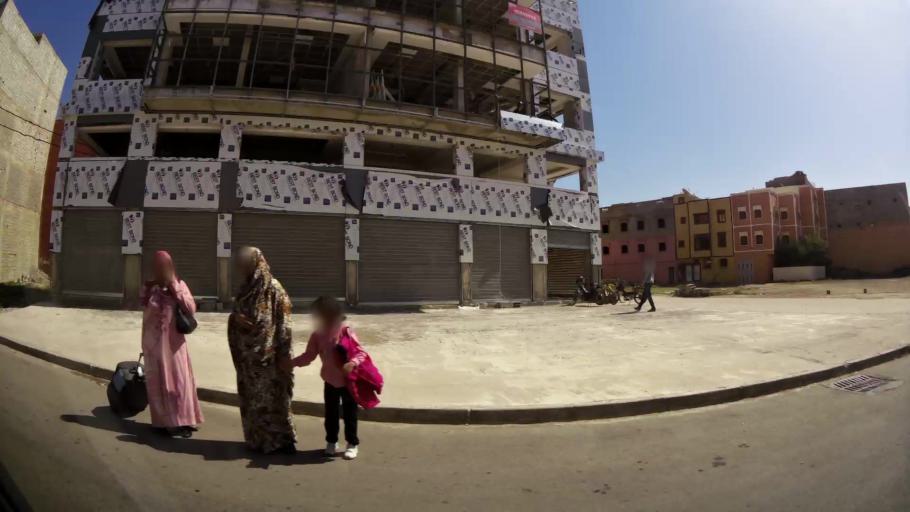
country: MA
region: Souss-Massa-Draa
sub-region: Inezgane-Ait Mellou
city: Inezgane
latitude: 30.3388
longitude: -9.5052
